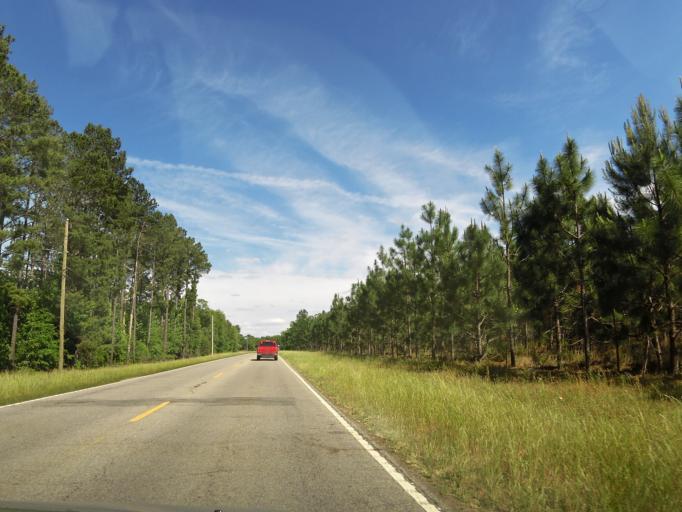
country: US
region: South Carolina
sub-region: Bamberg County
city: Denmark
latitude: 33.3354
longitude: -81.1638
